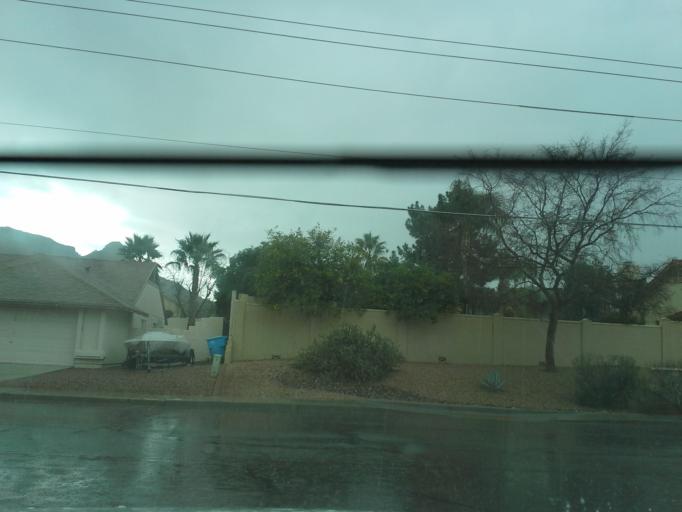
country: US
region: Arizona
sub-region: Maricopa County
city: Paradise Valley
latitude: 33.6332
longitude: -112.0525
